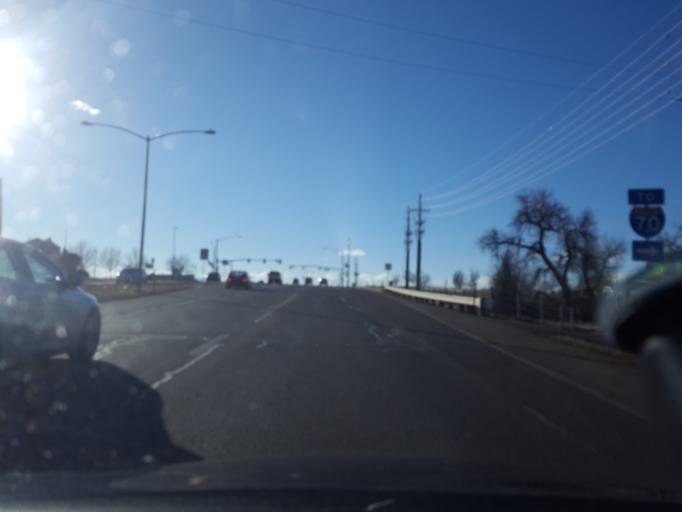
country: US
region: Colorado
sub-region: Adams County
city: Aurora
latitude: 39.7403
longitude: -104.7888
